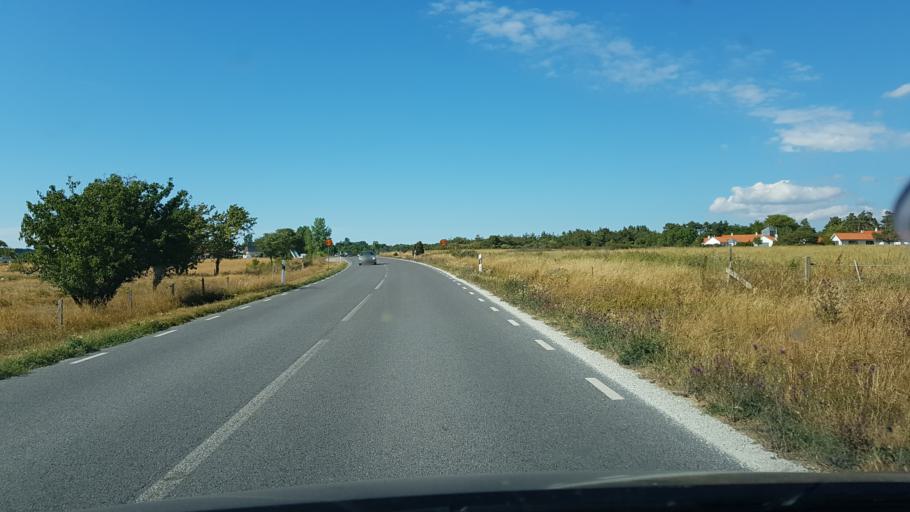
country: SE
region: Gotland
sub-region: Gotland
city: Klintehamn
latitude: 57.4268
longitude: 18.1497
